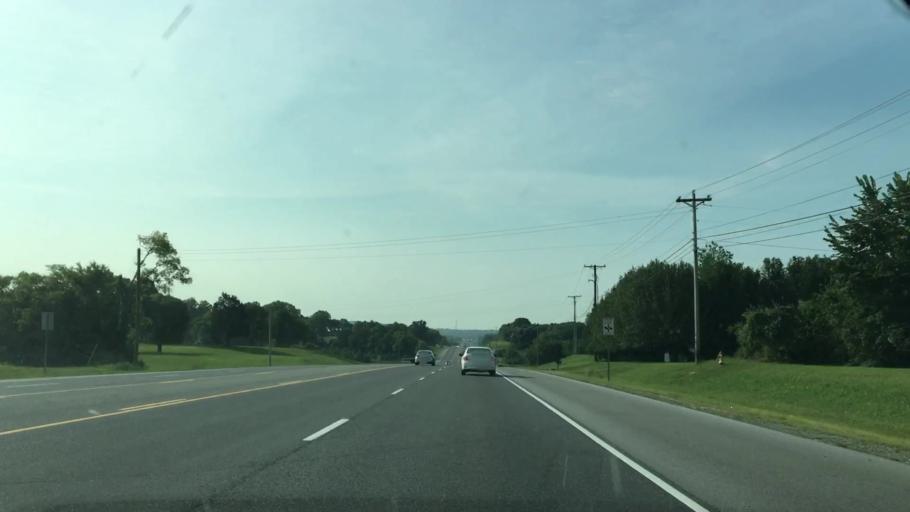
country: US
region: Tennessee
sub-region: Wilson County
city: Mount Juliet
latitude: 36.2052
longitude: -86.4185
